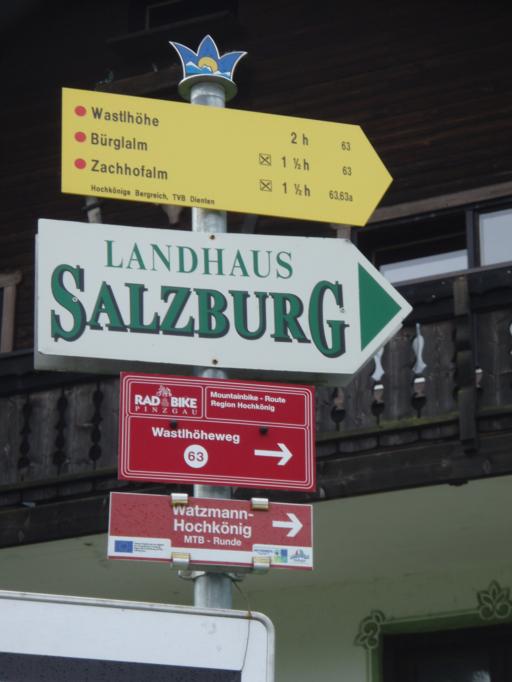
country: AT
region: Salzburg
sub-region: Politischer Bezirk Zell am See
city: Dienten am Hochkonig
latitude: 47.3855
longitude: 13.0178
